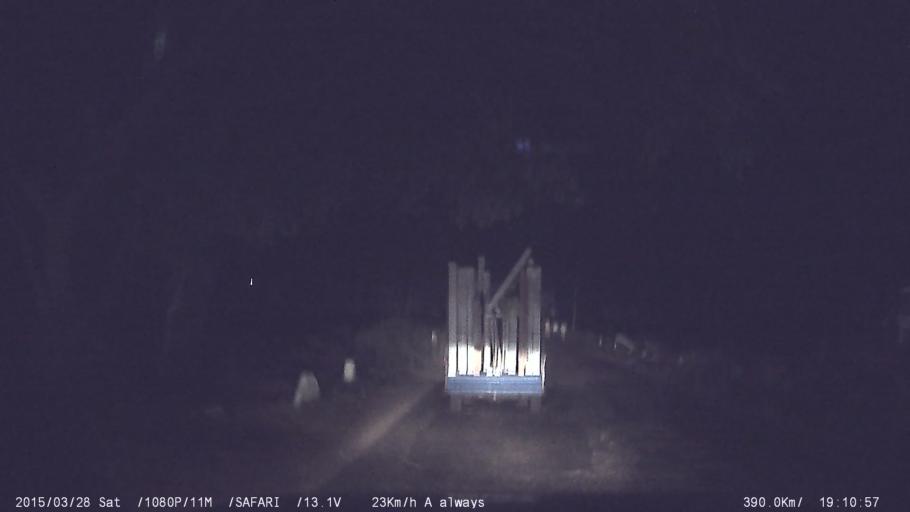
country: IN
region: Karnataka
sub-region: Mandya
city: Shrirangapattana
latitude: 12.3930
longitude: 76.6292
